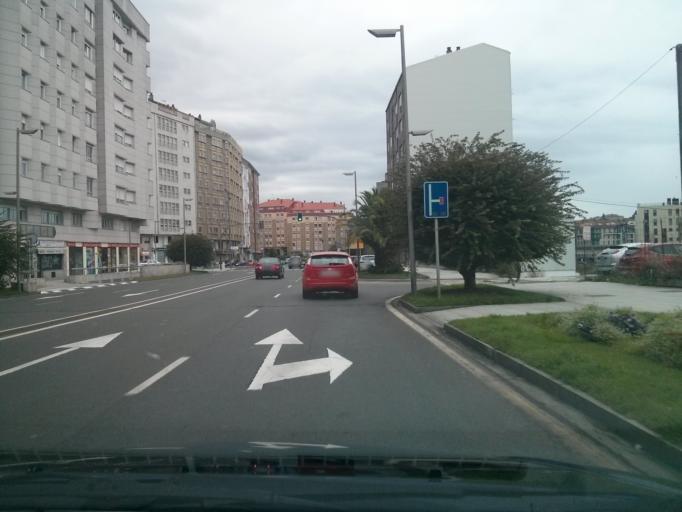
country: ES
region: Galicia
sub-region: Provincia da Coruna
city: Santiago de Compostela
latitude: 42.8710
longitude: -8.5504
